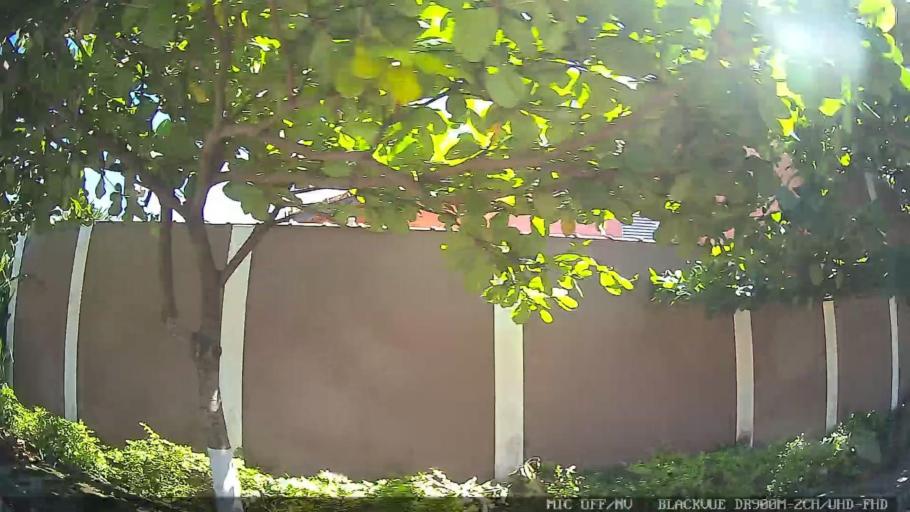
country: BR
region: Sao Paulo
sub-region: Peruibe
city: Peruibe
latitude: -24.3030
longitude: -46.9754
